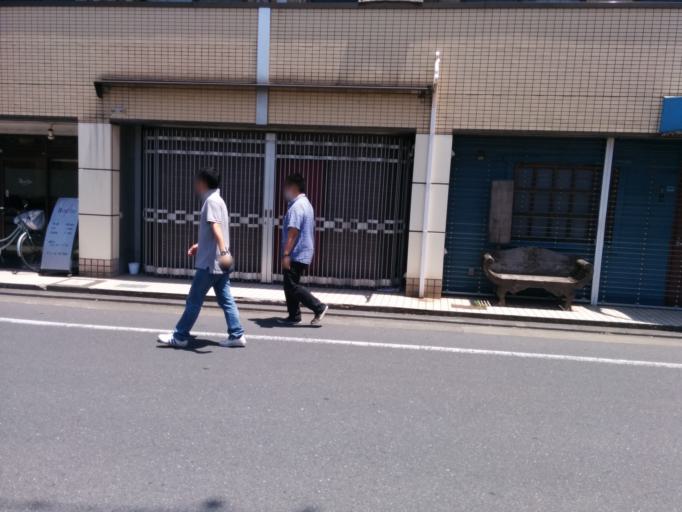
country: JP
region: Tokyo
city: Higashimurayama-shi
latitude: 35.7638
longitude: 139.4664
